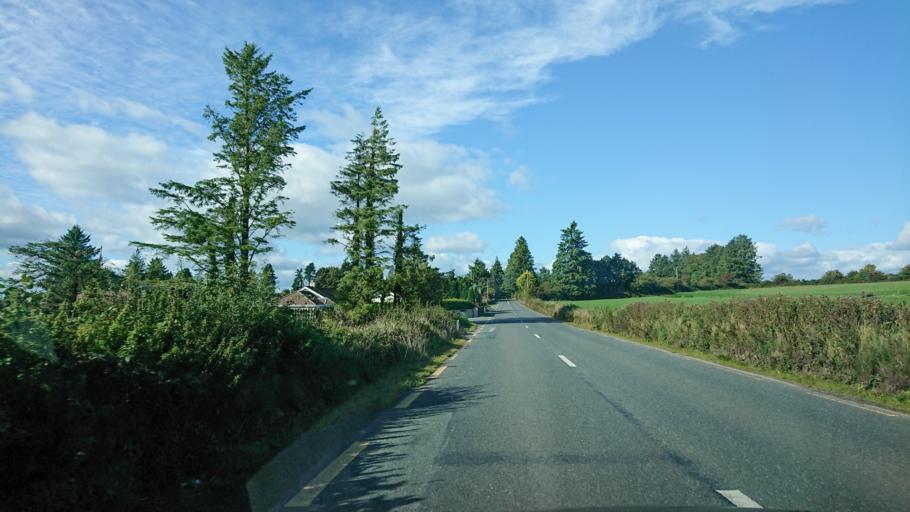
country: IE
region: Munster
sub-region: Waterford
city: Dungarvan
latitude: 52.1921
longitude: -7.6979
